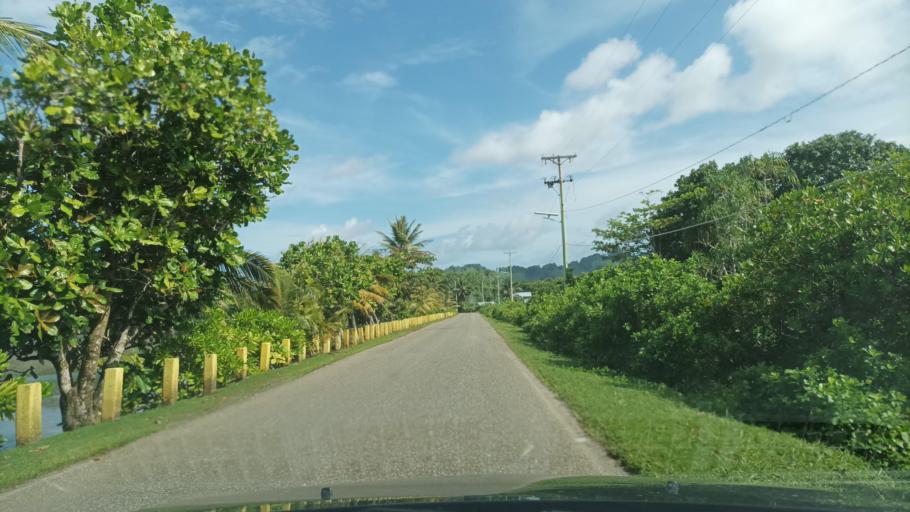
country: FM
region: Kosrae
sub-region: Lelu Municipality
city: Lelu
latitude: 5.3368
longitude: 163.0211
